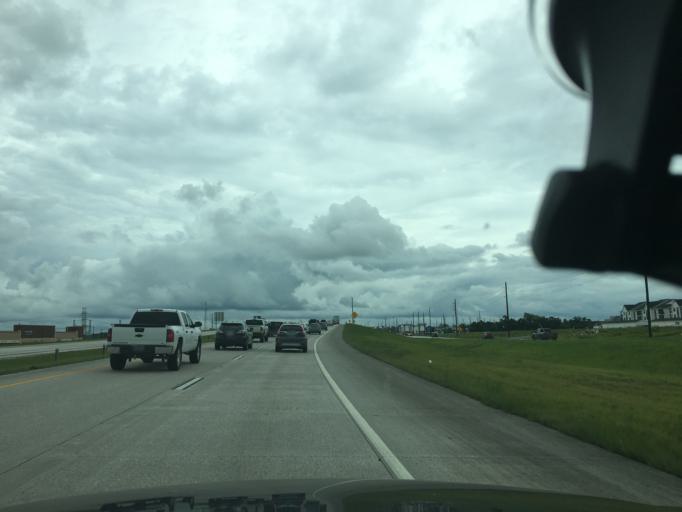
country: US
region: Texas
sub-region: Harris County
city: Tomball
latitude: 30.0855
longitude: -95.5327
